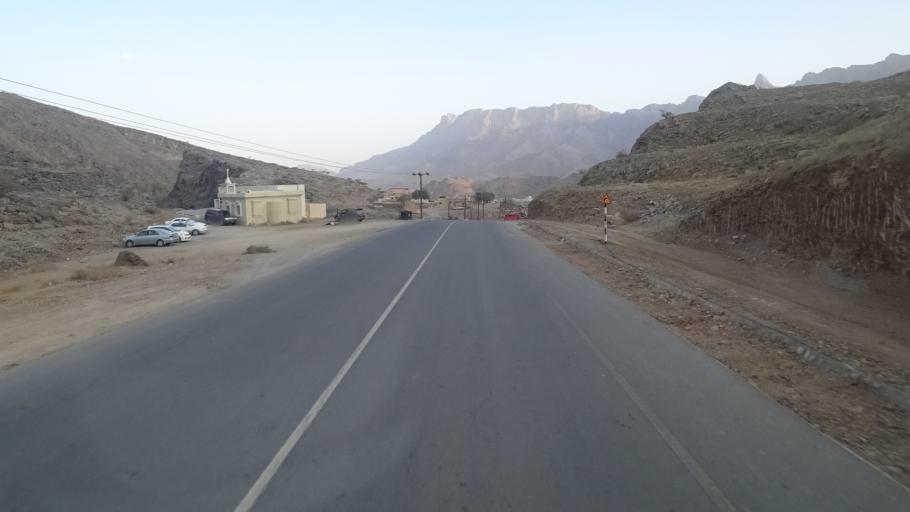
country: OM
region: Muhafazat ad Dakhiliyah
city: Bahla'
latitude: 23.1850
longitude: 57.1408
